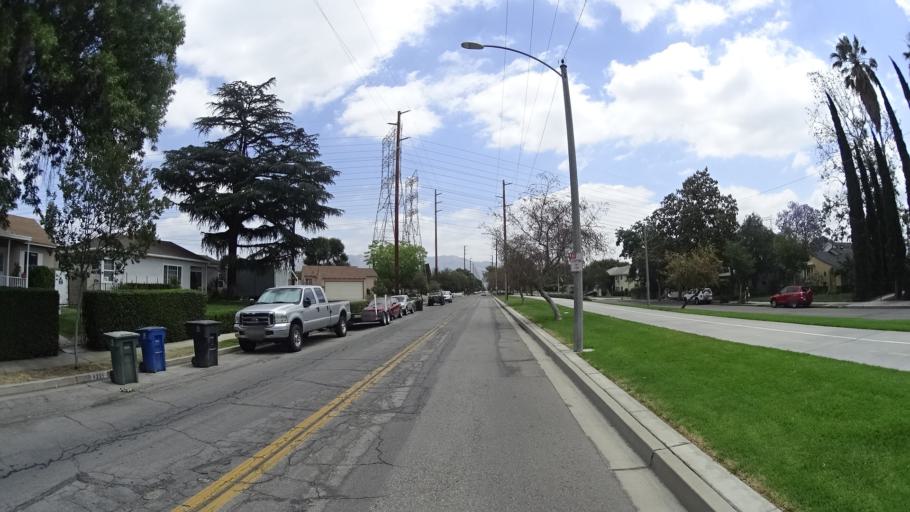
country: US
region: California
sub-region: Los Angeles County
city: North Hollywood
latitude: 34.1694
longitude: -118.3547
